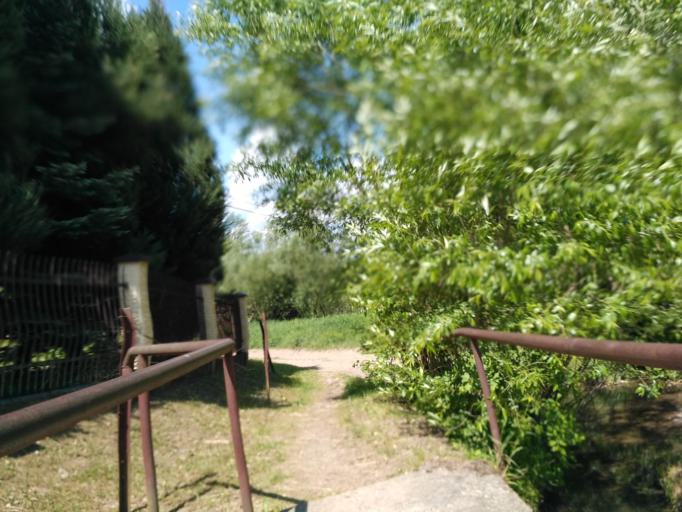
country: PL
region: Subcarpathian Voivodeship
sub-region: Powiat krosnienski
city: Dukla
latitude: 49.5973
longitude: 21.7111
